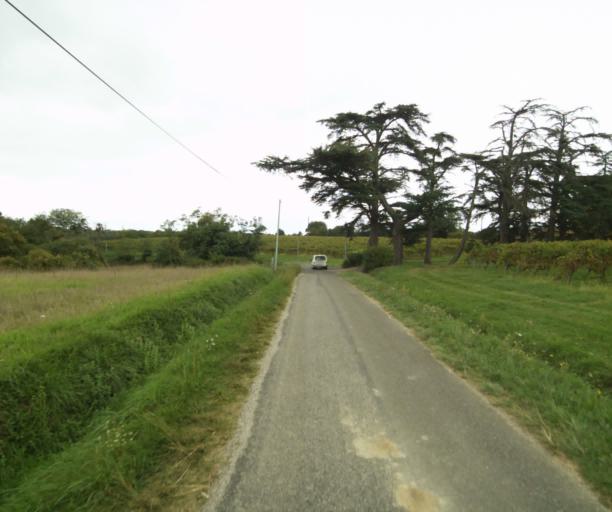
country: FR
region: Midi-Pyrenees
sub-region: Departement du Gers
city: Eauze
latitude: 43.8970
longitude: 0.0655
